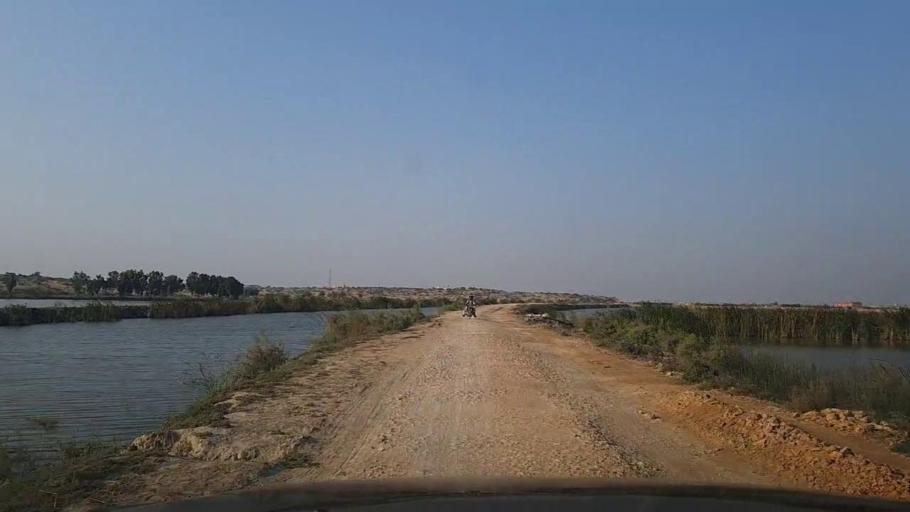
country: PK
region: Sindh
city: Thatta
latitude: 24.7347
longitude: 67.9066
